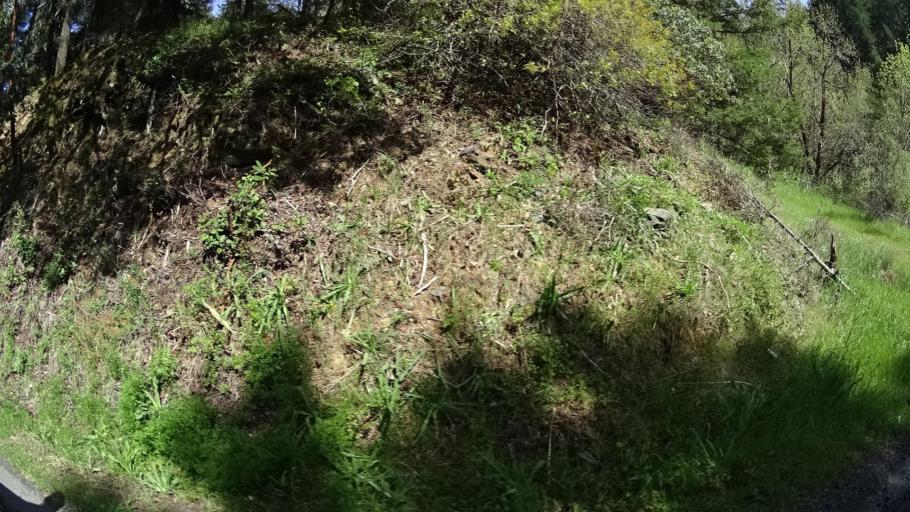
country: US
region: California
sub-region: Humboldt County
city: Redway
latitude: 40.3082
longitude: -123.6545
